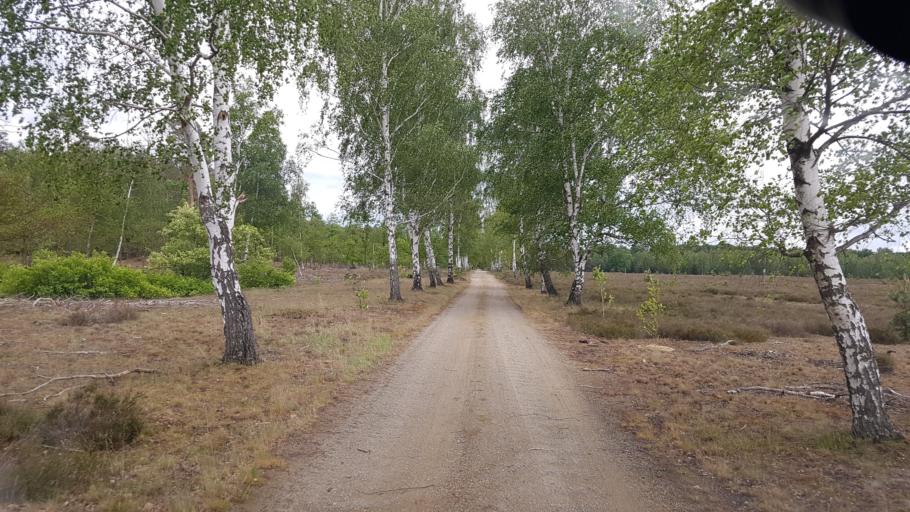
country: DE
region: Brandenburg
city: Hohenleipisch
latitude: 51.5347
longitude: 13.5382
